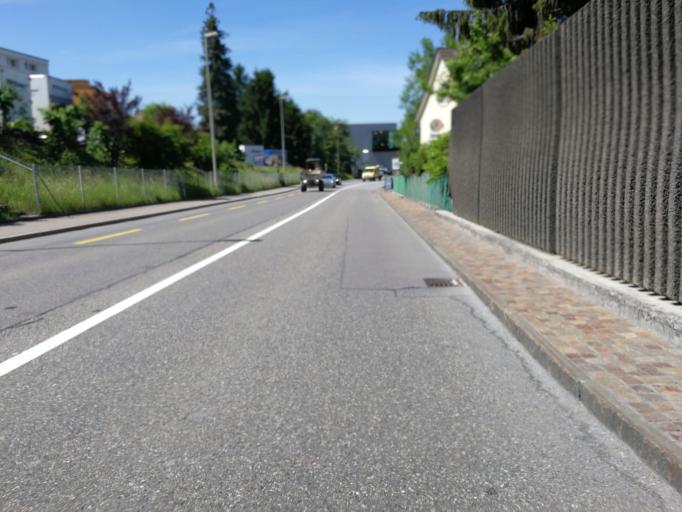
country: CH
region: Zurich
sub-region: Bezirk Horgen
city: Horgen / Allmend
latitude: 47.2465
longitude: 8.6066
